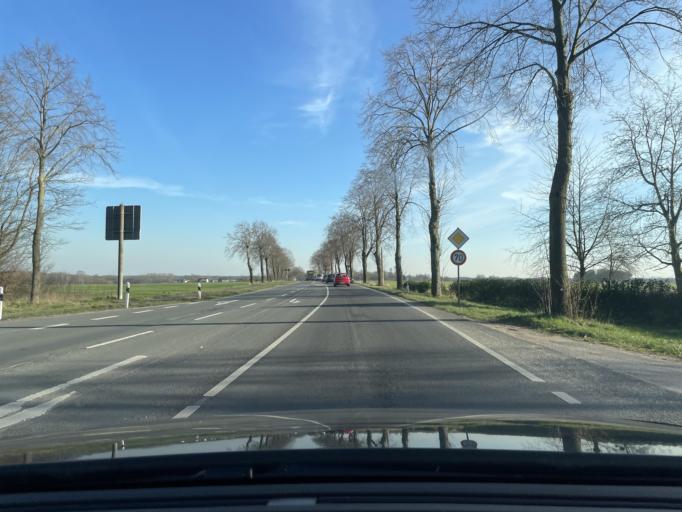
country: DE
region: North Rhine-Westphalia
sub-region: Regierungsbezirk Dusseldorf
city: Bruggen
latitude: 51.2235
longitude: 6.2015
